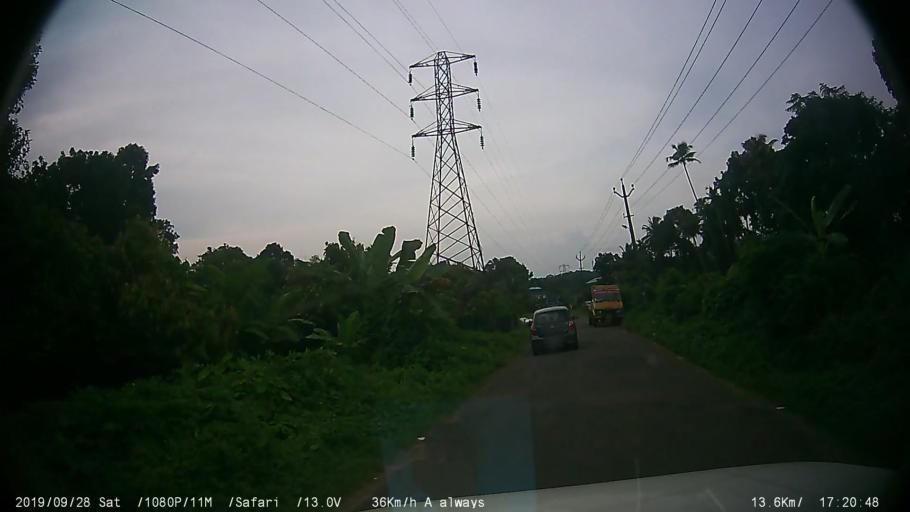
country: IN
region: Kerala
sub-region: Kottayam
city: Palackattumala
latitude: 9.7548
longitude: 76.5603
